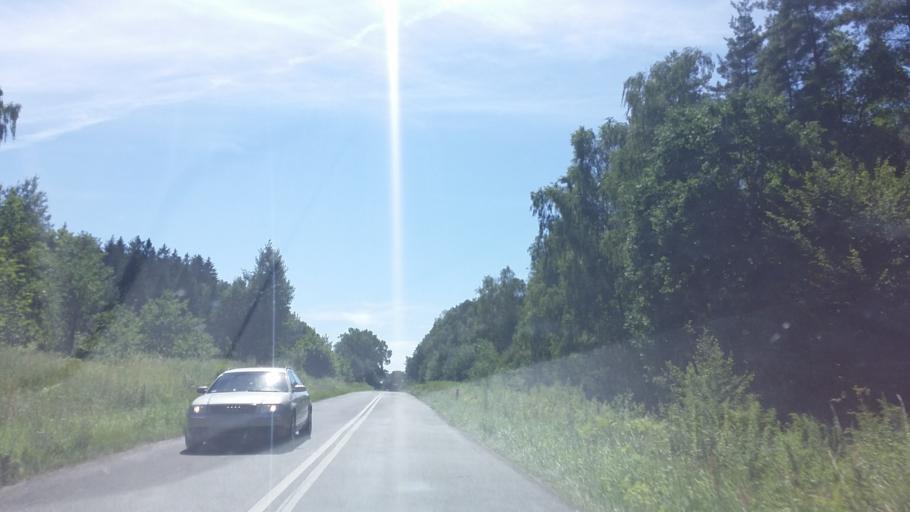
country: PL
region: West Pomeranian Voivodeship
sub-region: Powiat lobeski
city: Lobez
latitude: 53.6624
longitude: 15.6518
